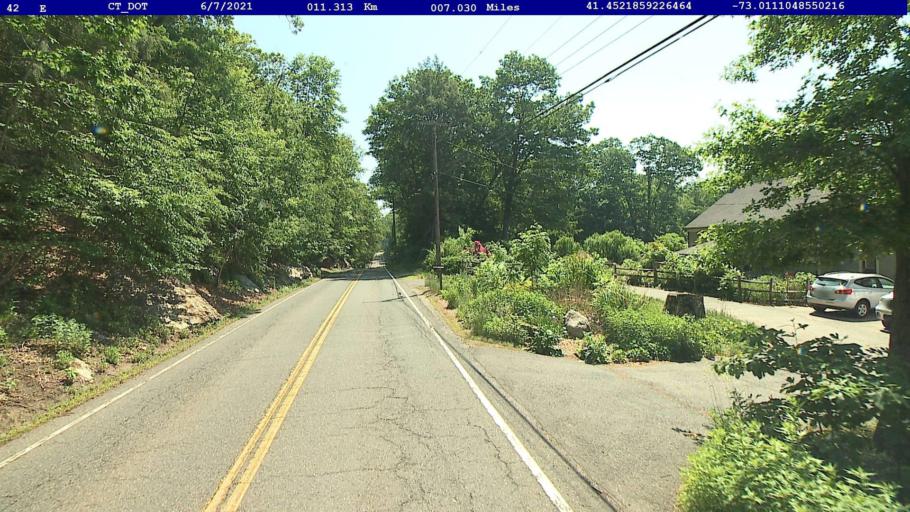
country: US
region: Connecticut
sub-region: New Haven County
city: Naugatuck
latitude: 41.4522
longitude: -73.0111
